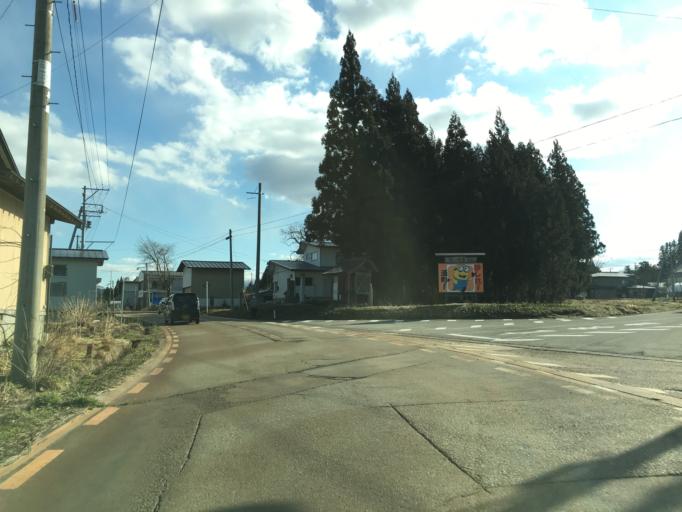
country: JP
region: Yamagata
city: Yonezawa
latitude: 37.9622
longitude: 139.9891
